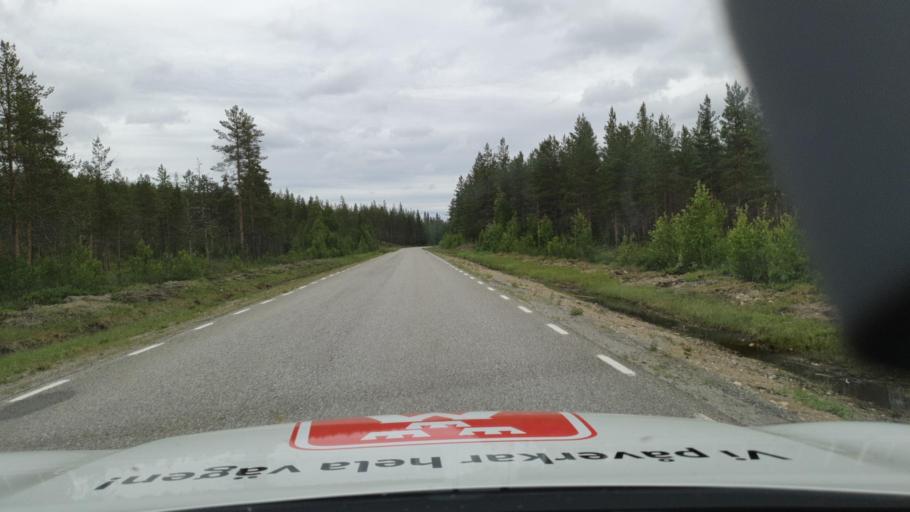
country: SE
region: Vaesterbotten
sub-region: Lycksele Kommun
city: Lycksele
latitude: 64.1810
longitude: 18.3176
